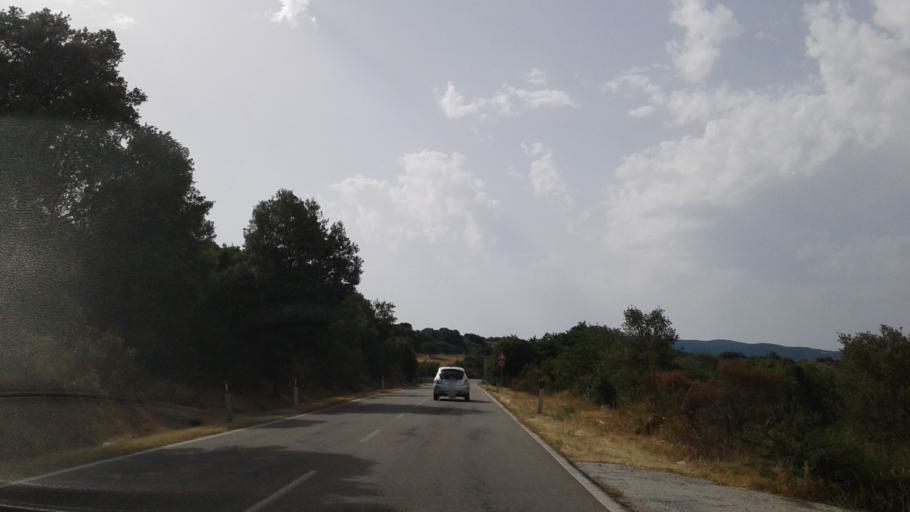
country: IT
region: Sardinia
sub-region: Provincia di Olbia-Tempio
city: Sant'Antonio di Gallura
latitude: 40.9704
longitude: 9.2722
